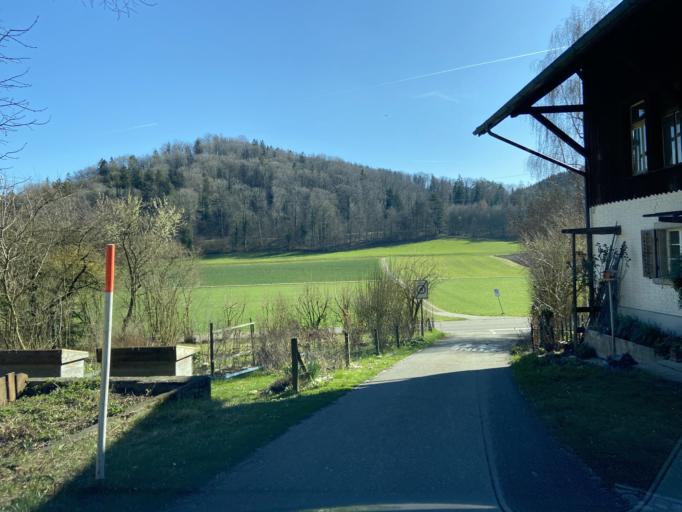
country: CH
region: Zurich
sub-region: Bezirk Winterthur
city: Wuelflingen (Kreis 6) / Niederfeld
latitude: 47.4966
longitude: 8.6795
